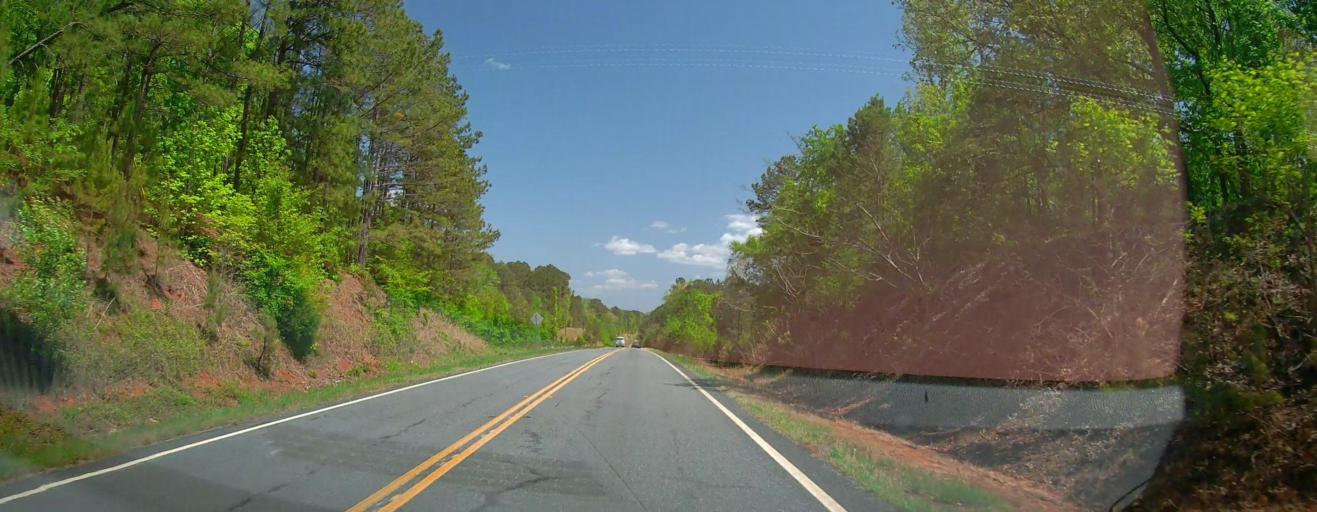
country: US
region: Georgia
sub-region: Putnam County
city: Eatonton
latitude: 33.2078
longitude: -83.4726
